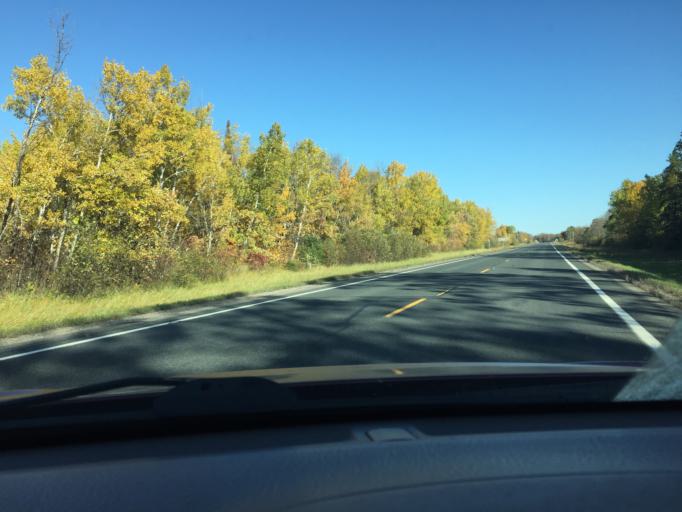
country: US
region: Minnesota
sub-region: Beltrami County
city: Redby
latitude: 48.1709
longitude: -94.5128
